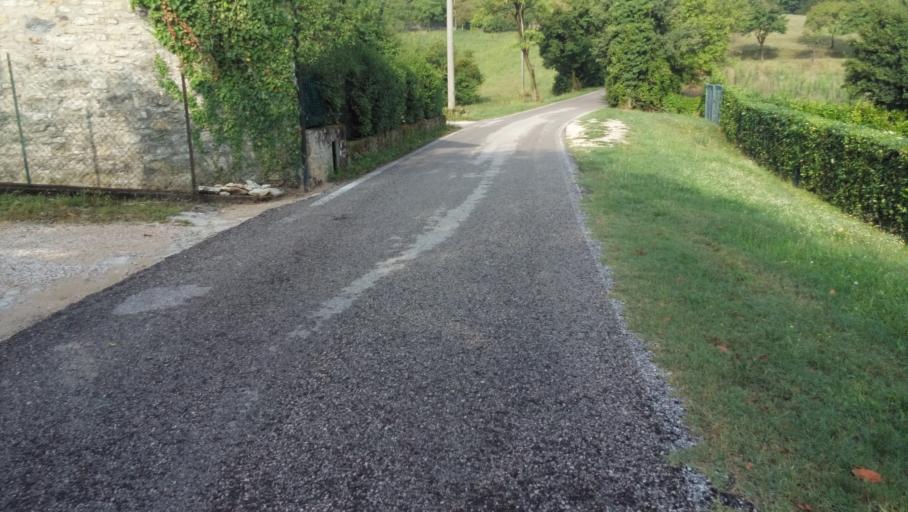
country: IT
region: Veneto
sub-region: Provincia di Vicenza
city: Monteviale
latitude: 45.5494
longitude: 11.4636
